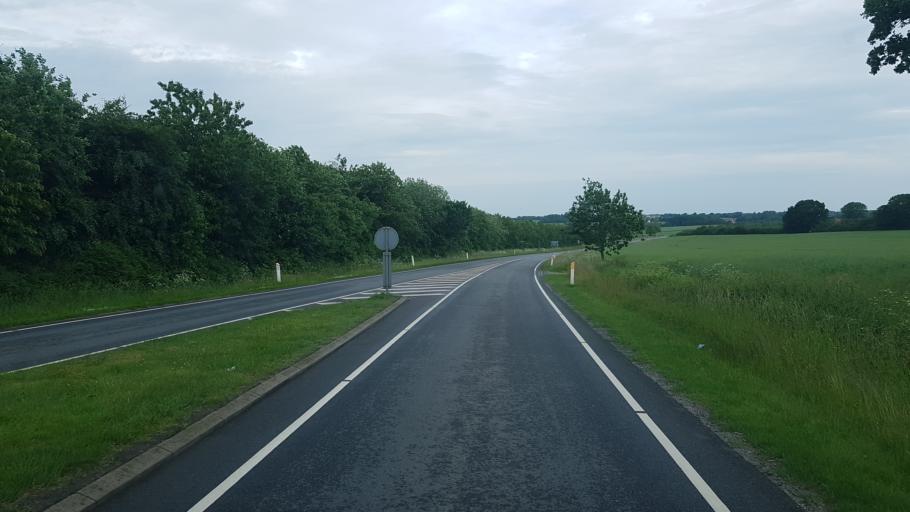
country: DK
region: South Denmark
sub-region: Vejen Kommune
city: Rodding
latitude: 55.3770
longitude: 9.0606
